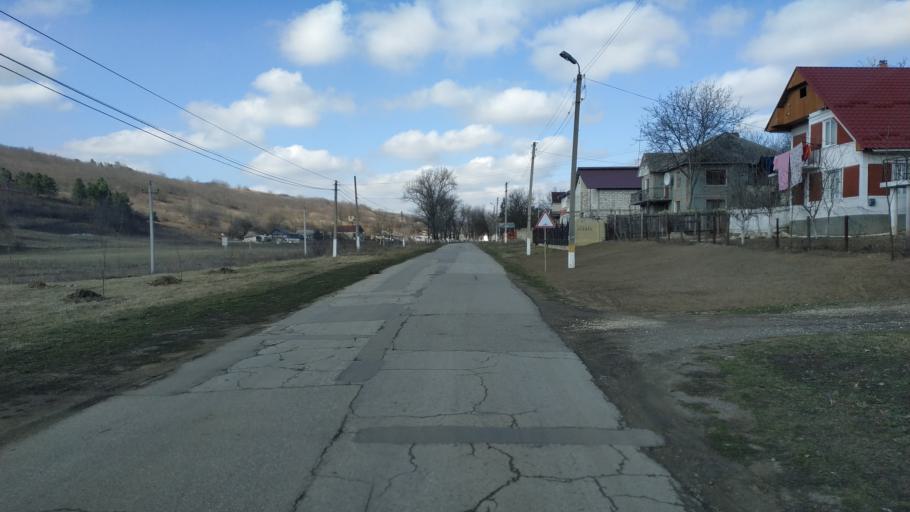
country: MD
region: Hincesti
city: Hincesti
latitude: 46.8720
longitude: 28.6344
